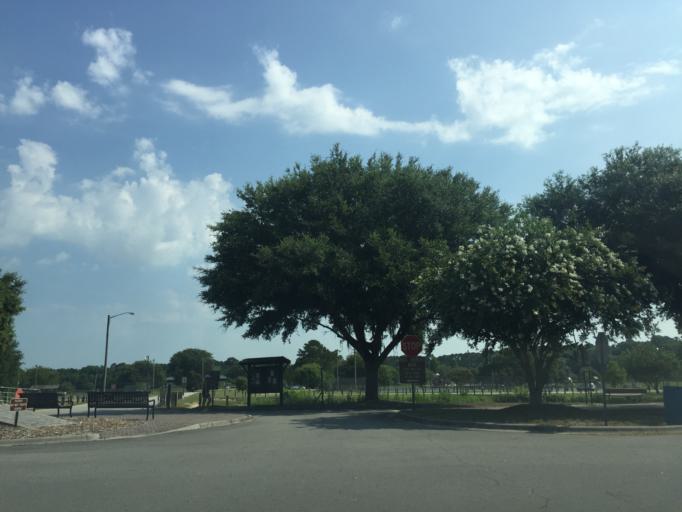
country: US
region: Georgia
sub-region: Chatham County
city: Isle of Hope
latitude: 31.9905
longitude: -81.0877
